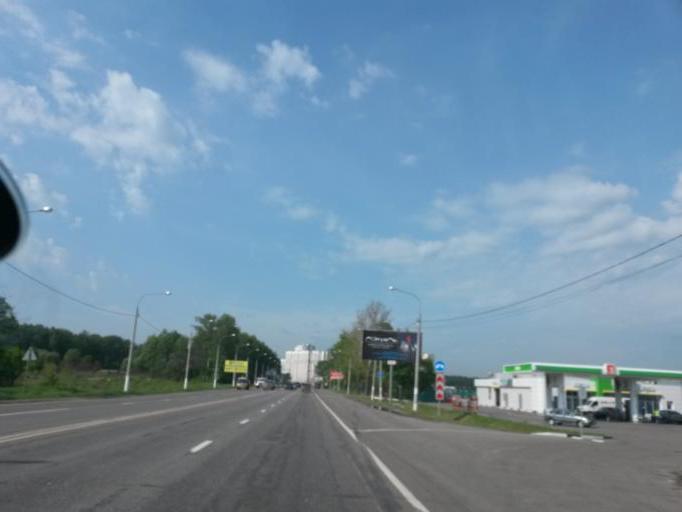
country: RU
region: Moskovskaya
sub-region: Chekhovskiy Rayon
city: Chekhov
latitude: 55.1769
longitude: 37.4803
